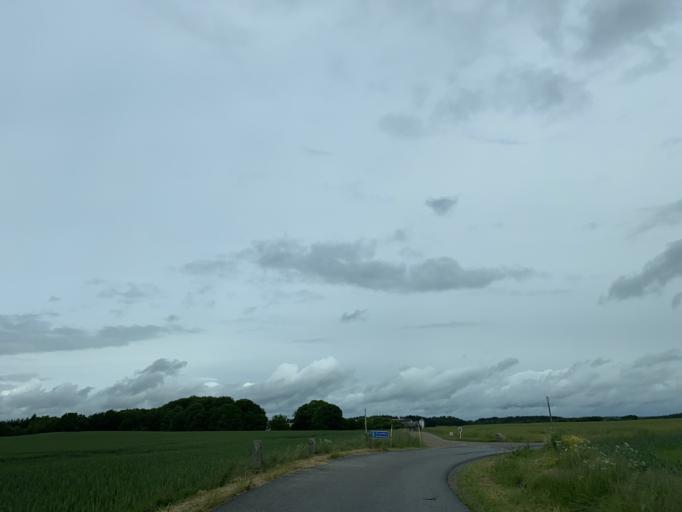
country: DK
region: Central Jutland
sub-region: Favrskov Kommune
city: Hammel
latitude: 56.2355
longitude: 9.7849
